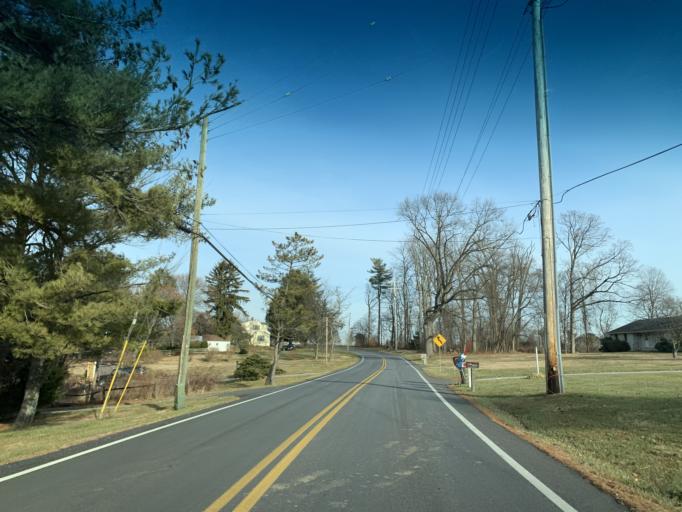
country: US
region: Maryland
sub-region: Carroll County
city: Hampstead
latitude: 39.6118
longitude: -76.8134
